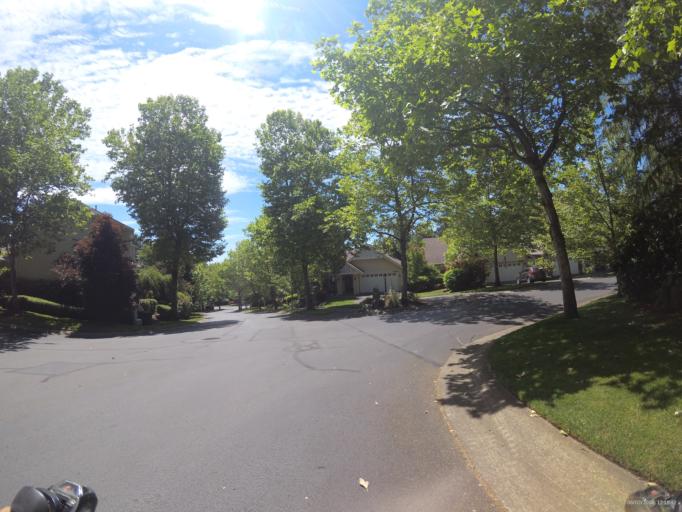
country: US
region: Washington
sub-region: Pierce County
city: University Place
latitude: 47.2030
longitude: -122.5494
